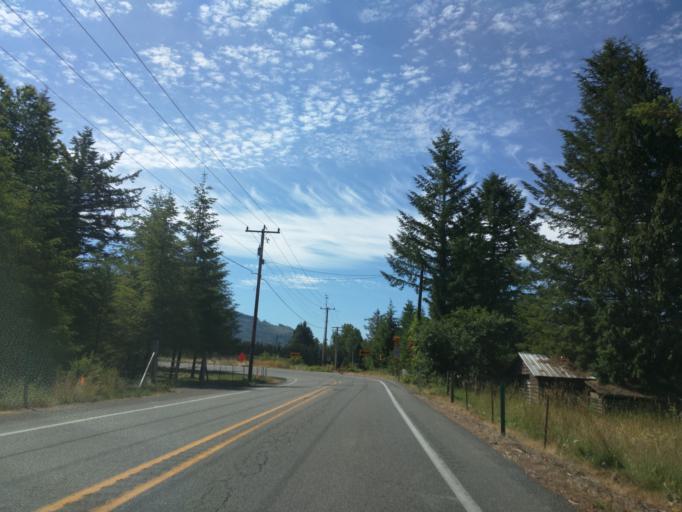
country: US
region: Washington
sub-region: Whatcom County
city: Peaceful Valley
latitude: 48.9180
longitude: -122.1433
